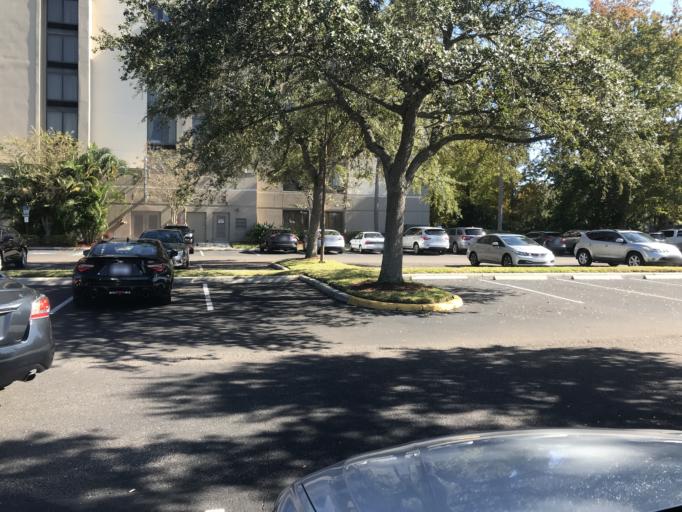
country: US
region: Florida
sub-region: Hillsborough County
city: Egypt Lake-Leto
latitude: 27.9574
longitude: -82.5264
